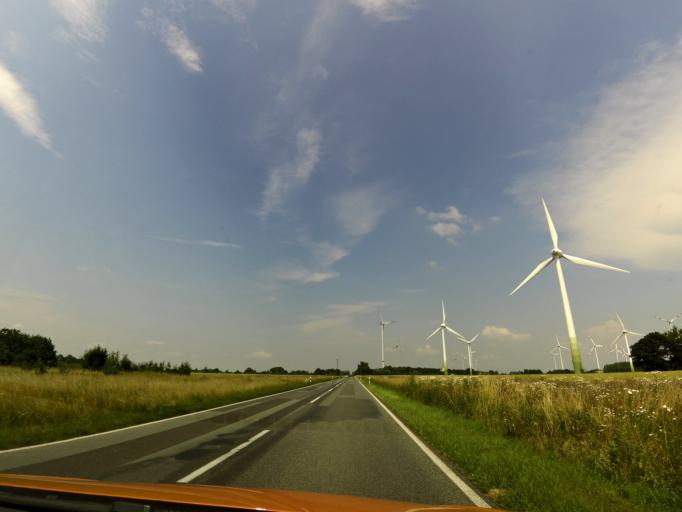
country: DE
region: Brandenburg
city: Gerdshagen
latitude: 53.2211
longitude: 12.2050
